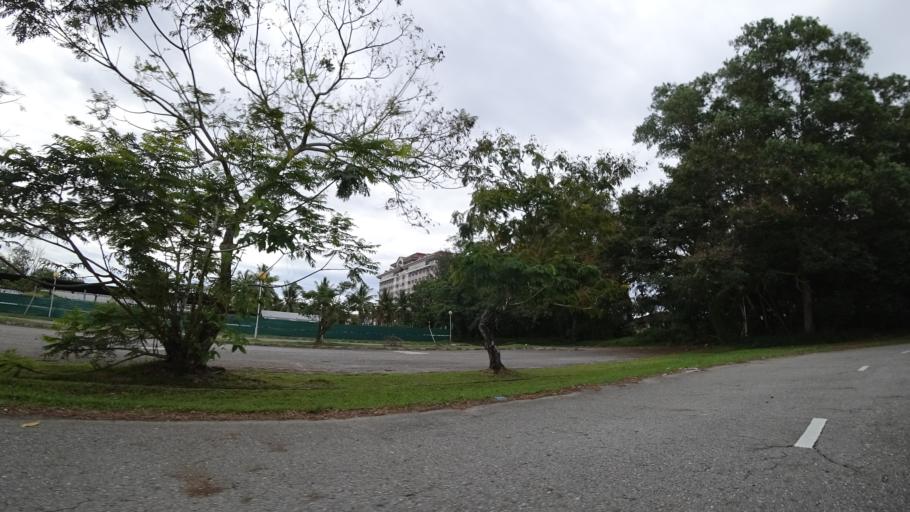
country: BN
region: Brunei and Muara
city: Bandar Seri Begawan
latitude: 4.9319
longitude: 114.9465
